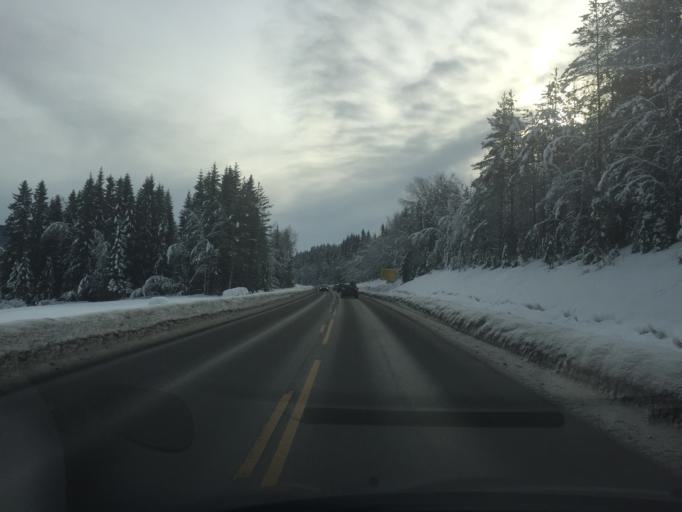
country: NO
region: Hedmark
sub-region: Trysil
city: Innbygda
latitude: 61.2743
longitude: 12.2915
